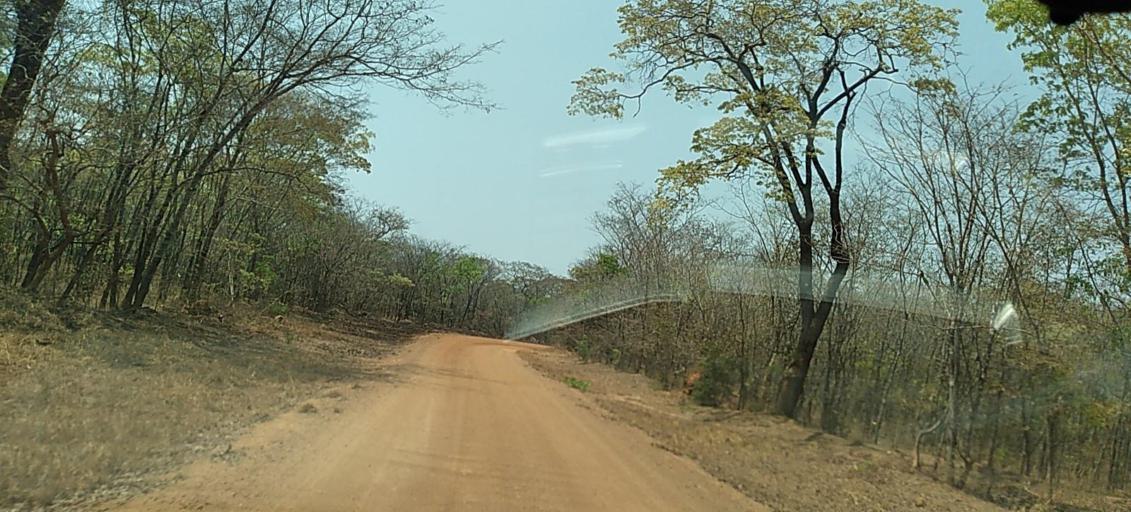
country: ZM
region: Central
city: Mumbwa
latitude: -14.2647
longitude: 26.5165
